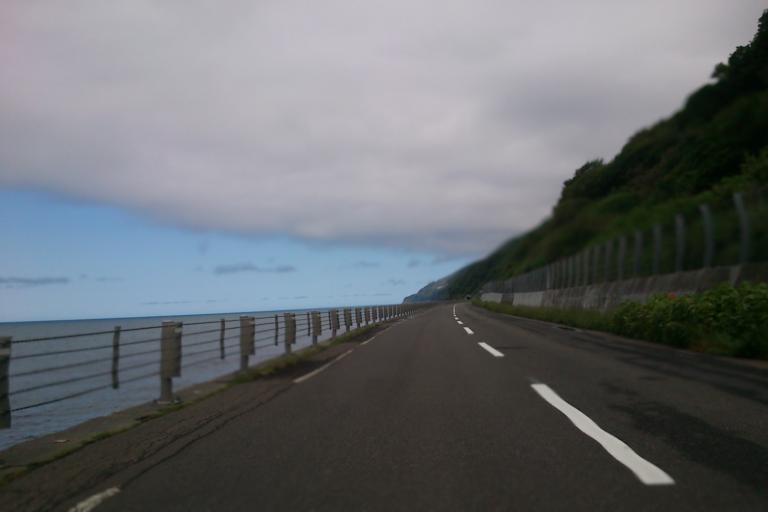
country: JP
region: Hokkaido
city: Ishikari
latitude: 43.4275
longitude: 141.4228
